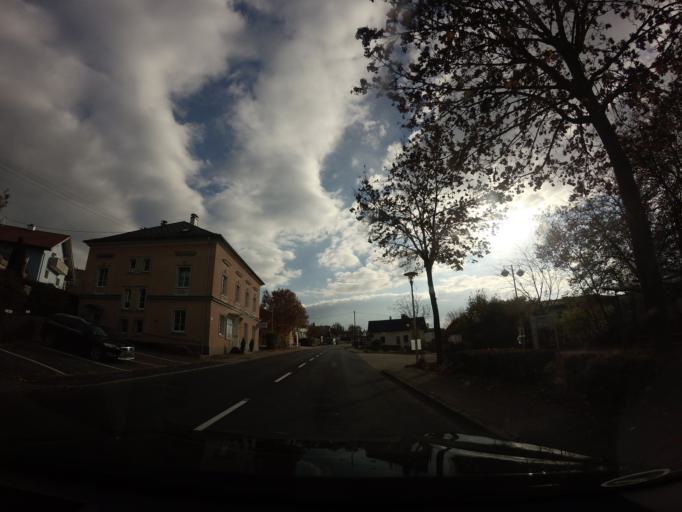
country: AT
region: Upper Austria
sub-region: Politischer Bezirk Urfahr-Umgebung
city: Zwettl an der Rodl
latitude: 48.4640
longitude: 14.2717
